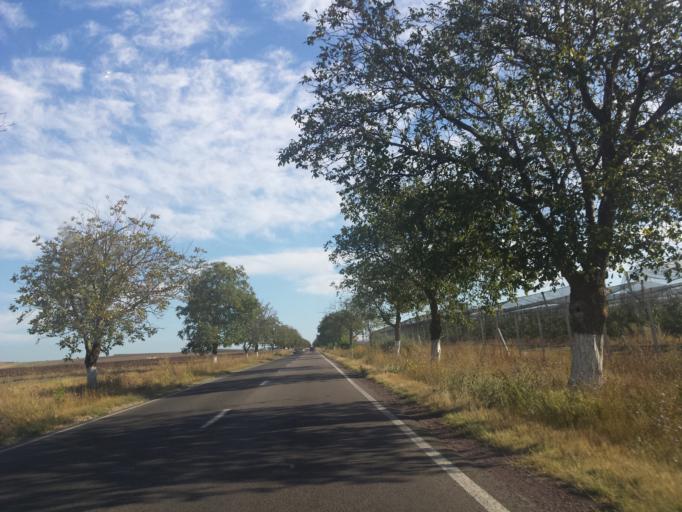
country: RO
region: Tulcea
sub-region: Comuna Frecatei
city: Cataloi
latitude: 45.1086
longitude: 28.7448
